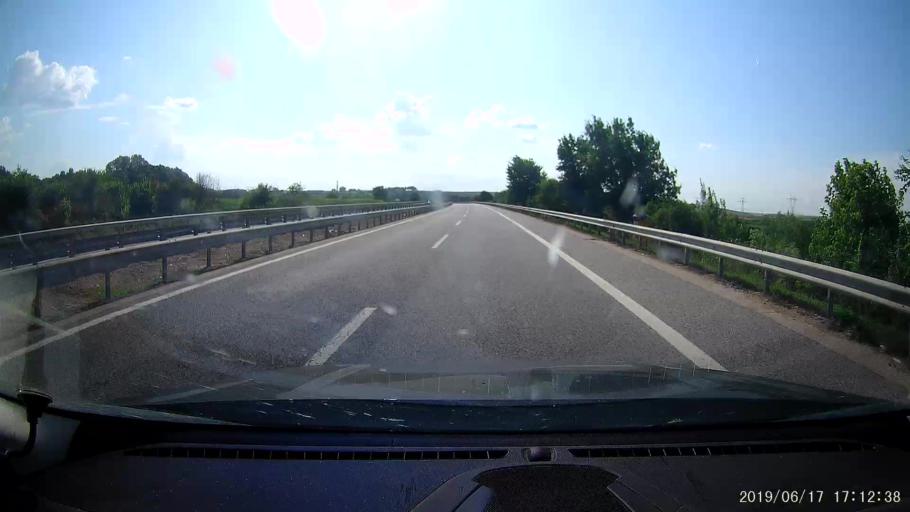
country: TR
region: Edirne
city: Edirne
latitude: 41.7006
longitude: 26.5583
